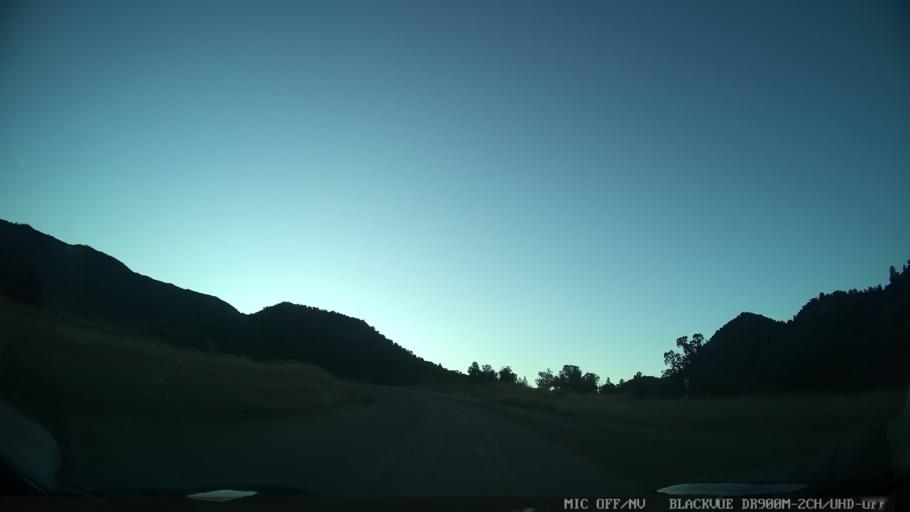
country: US
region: Colorado
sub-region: Eagle County
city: Edwards
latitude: 39.8574
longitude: -106.6451
